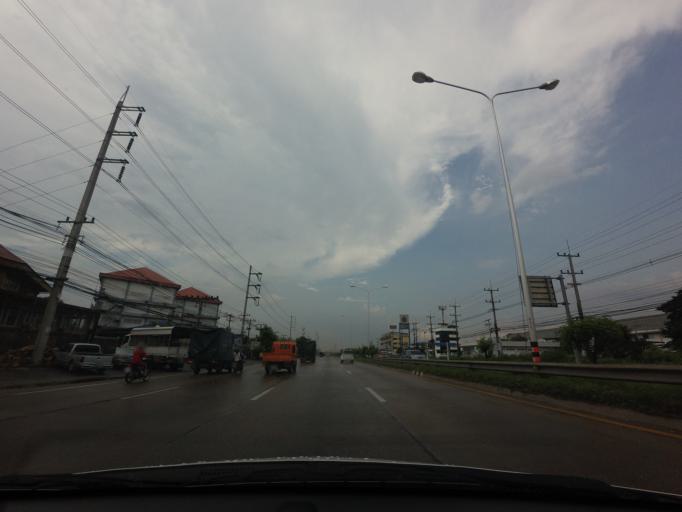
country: TH
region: Nakhon Pathom
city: Sam Phran
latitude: 13.7418
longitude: 100.2379
